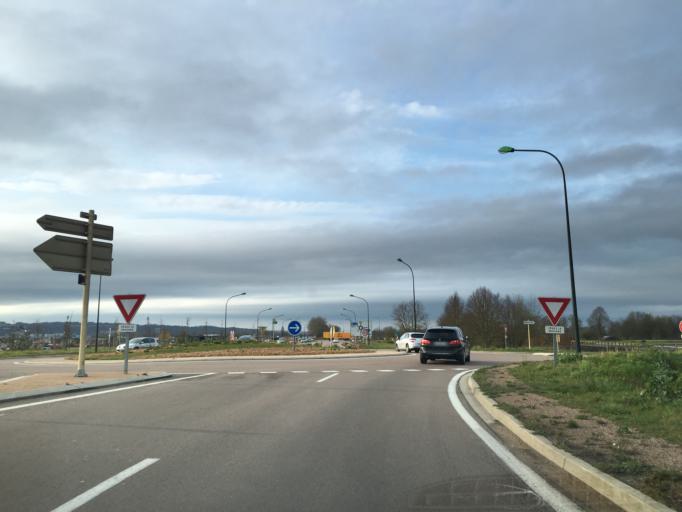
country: FR
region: Bourgogne
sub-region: Departement de l'Yonne
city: Maillot
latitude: 48.1717
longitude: 3.2956
